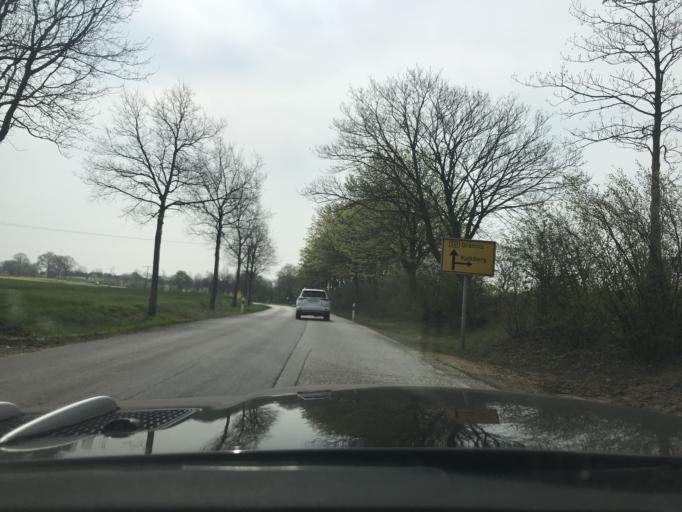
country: DE
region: Schleswig-Holstein
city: Heringsdorf
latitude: 54.2831
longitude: 11.0186
